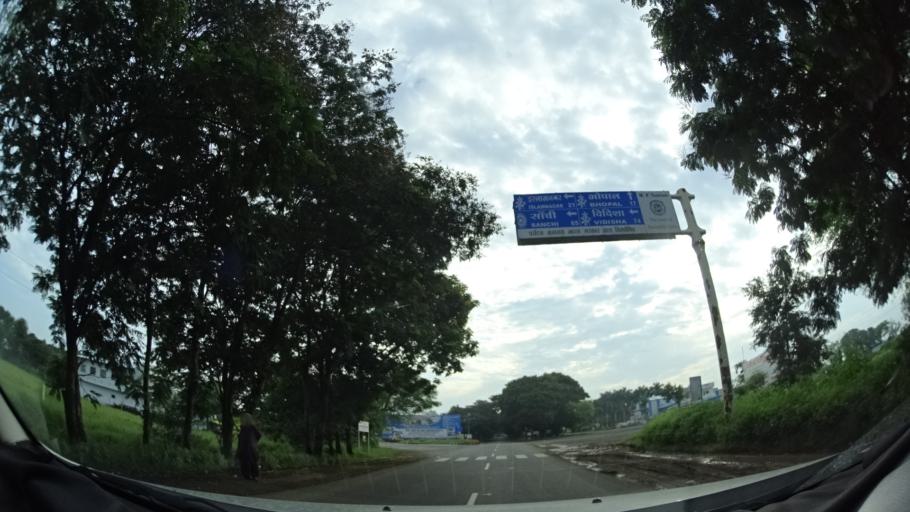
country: IN
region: Madhya Pradesh
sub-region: Bhopal
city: Bhopal
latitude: 23.2480
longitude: 77.2589
